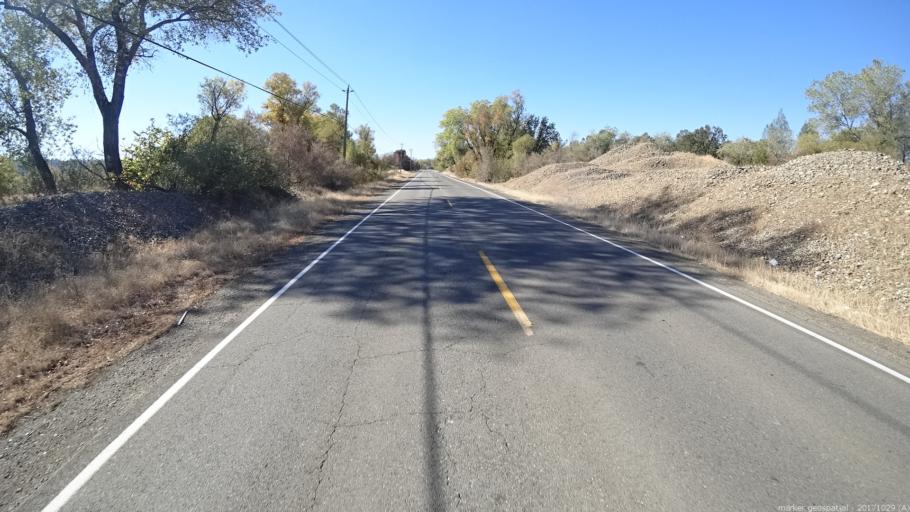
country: US
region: California
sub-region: Shasta County
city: Redding
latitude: 40.5014
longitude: -122.4362
